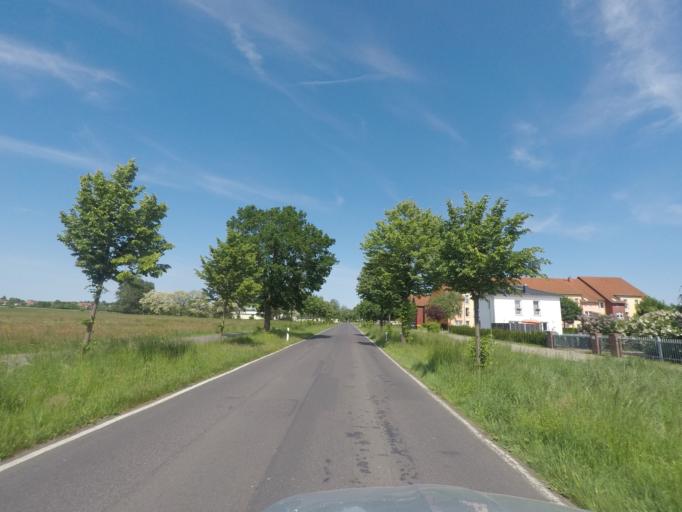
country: DE
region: Brandenburg
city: Britz
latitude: 52.8605
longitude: 13.7430
